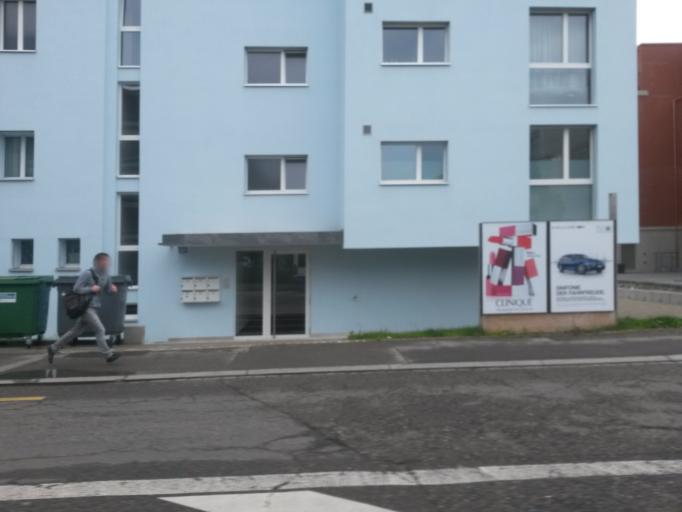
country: CH
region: Zurich
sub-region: Bezirk Zuerich
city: Zuerich (Kreis 11) / Oerlikon
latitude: 47.4133
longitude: 8.5321
